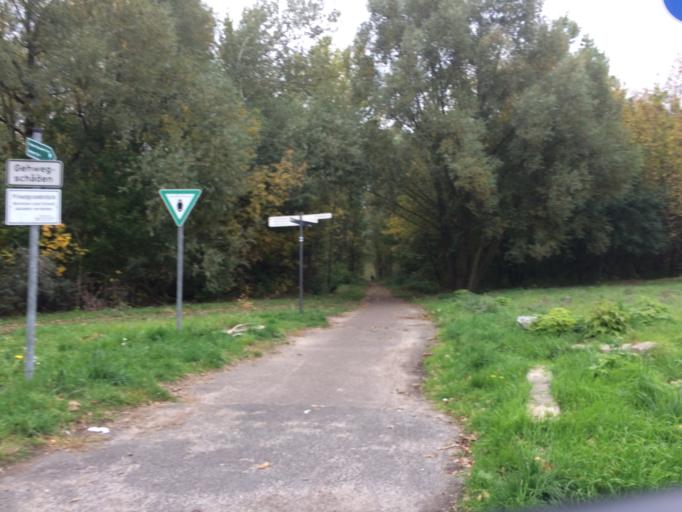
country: DE
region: Berlin
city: Rosenthal
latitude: 52.5997
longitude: 13.3716
